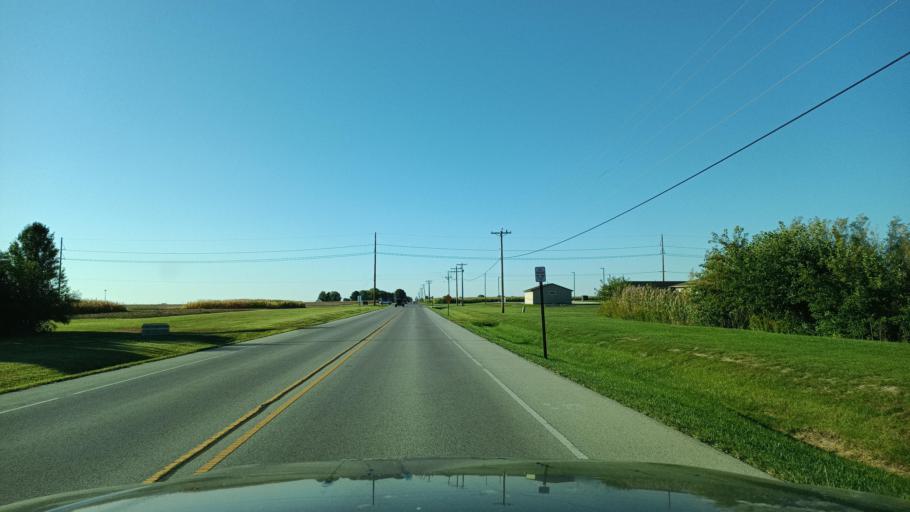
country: US
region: Illinois
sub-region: Champaign County
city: Savoy
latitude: 40.0566
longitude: -88.2384
